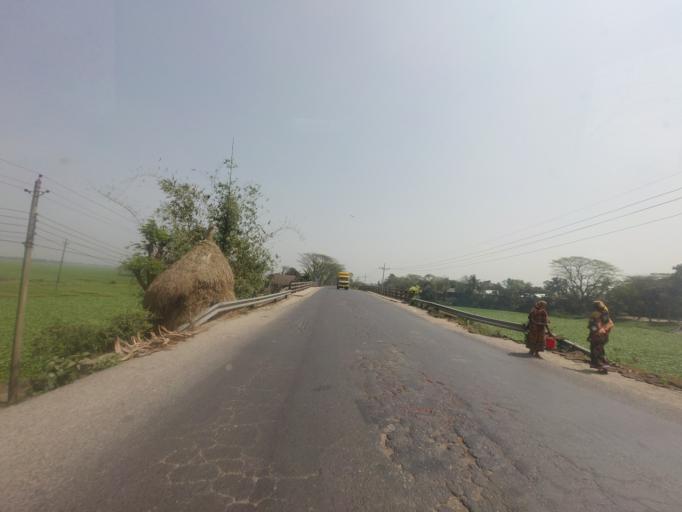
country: BD
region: Dhaka
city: Bhairab Bazar
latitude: 24.0541
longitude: 91.1502
